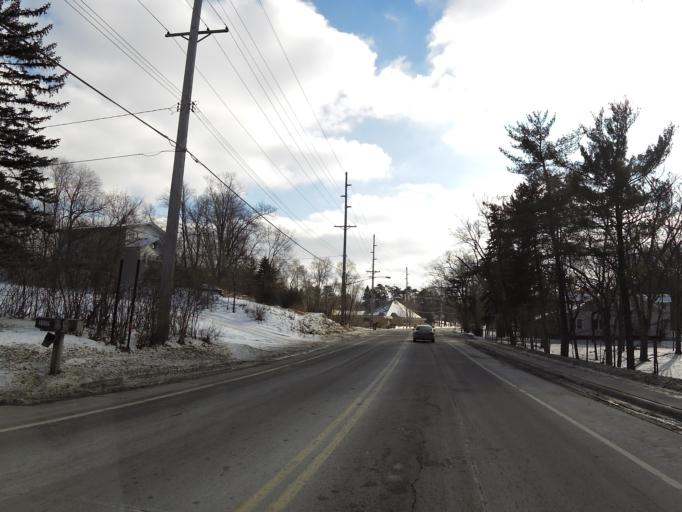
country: US
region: Minnesota
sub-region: Hennepin County
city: Hopkins
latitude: 44.9028
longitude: -93.4652
